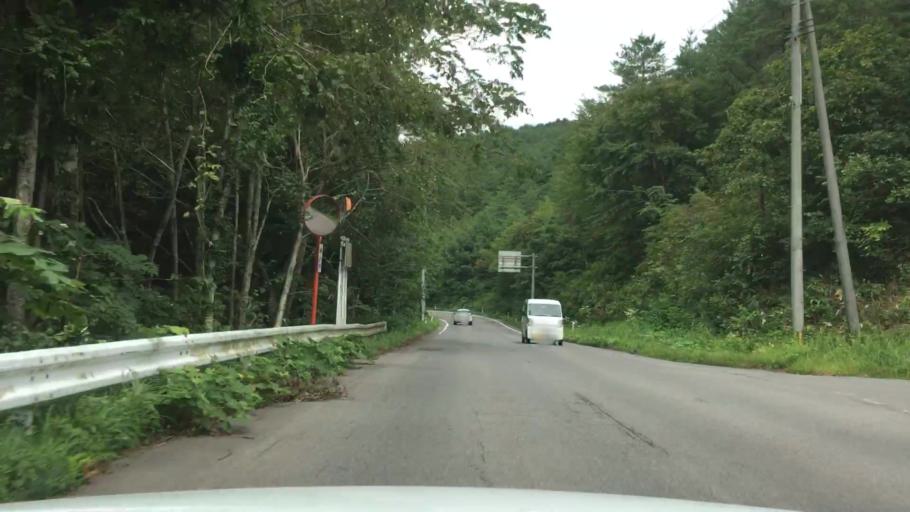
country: JP
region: Aomori
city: Shimokizukuri
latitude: 40.7208
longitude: 140.2584
